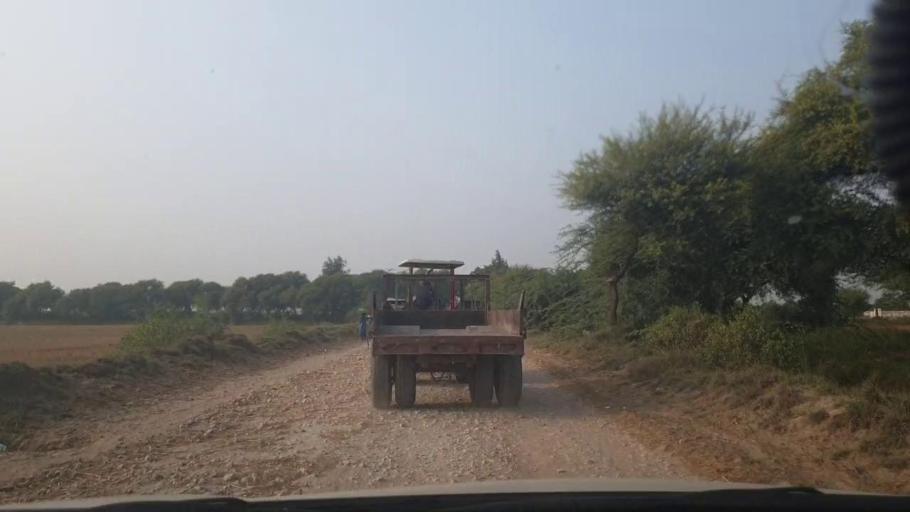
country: PK
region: Sindh
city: Bulri
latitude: 24.8038
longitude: 68.4121
